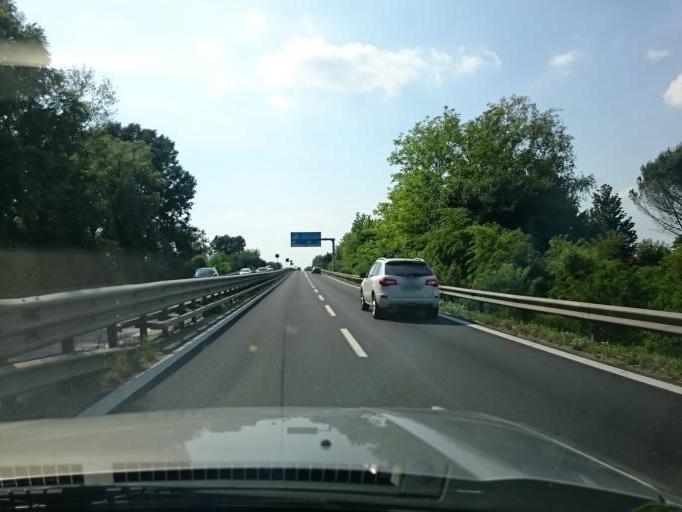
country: IT
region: Veneto
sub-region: Provincia di Padova
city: Mandriola-Sant'Agostino
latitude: 45.3795
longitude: 11.8342
